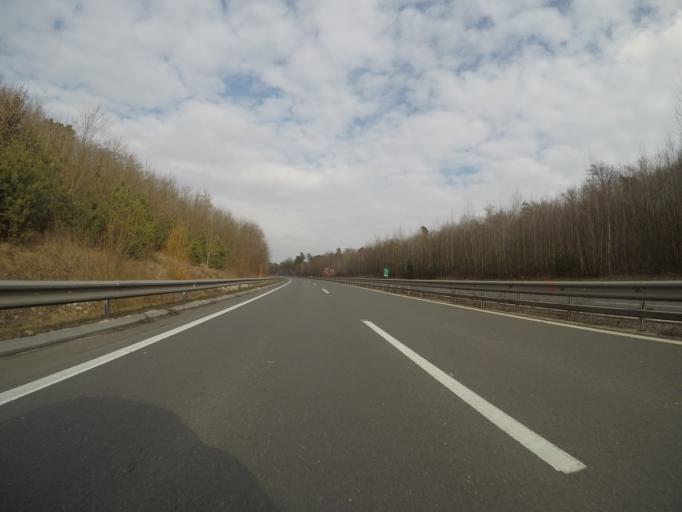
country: SI
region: Krizevci
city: Krizevci pri Ljutomeru
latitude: 46.5796
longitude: 16.0842
